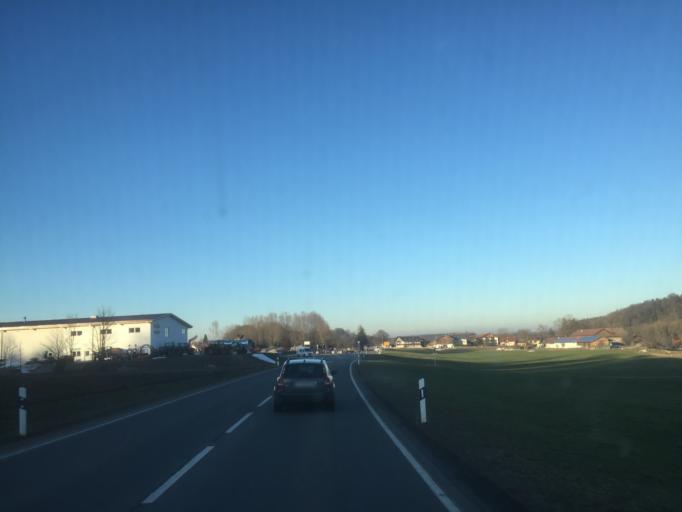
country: DE
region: Bavaria
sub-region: Upper Bavaria
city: Vachendorf
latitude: 47.8475
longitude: 12.6311
